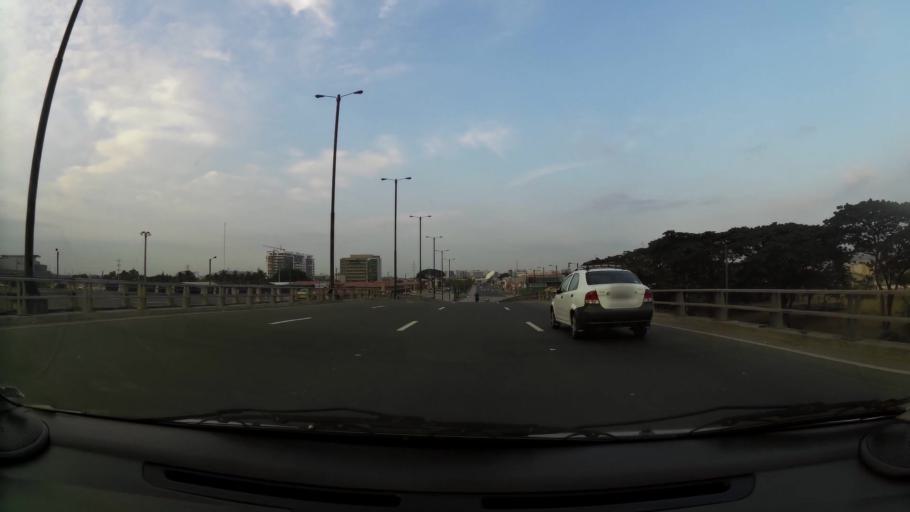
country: EC
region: Guayas
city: Eloy Alfaro
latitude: -2.1405
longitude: -79.8827
